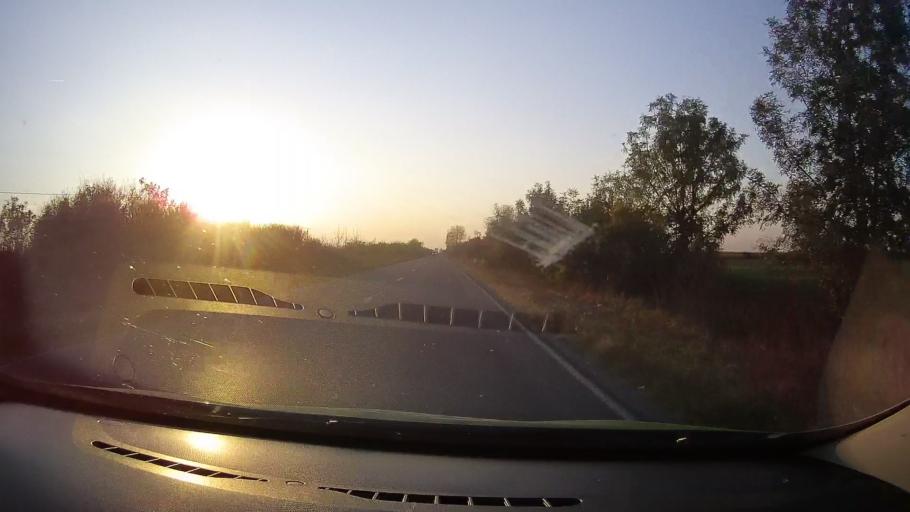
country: RO
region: Arad
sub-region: Comuna Ineu
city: Ineu
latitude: 46.4313
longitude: 21.8119
